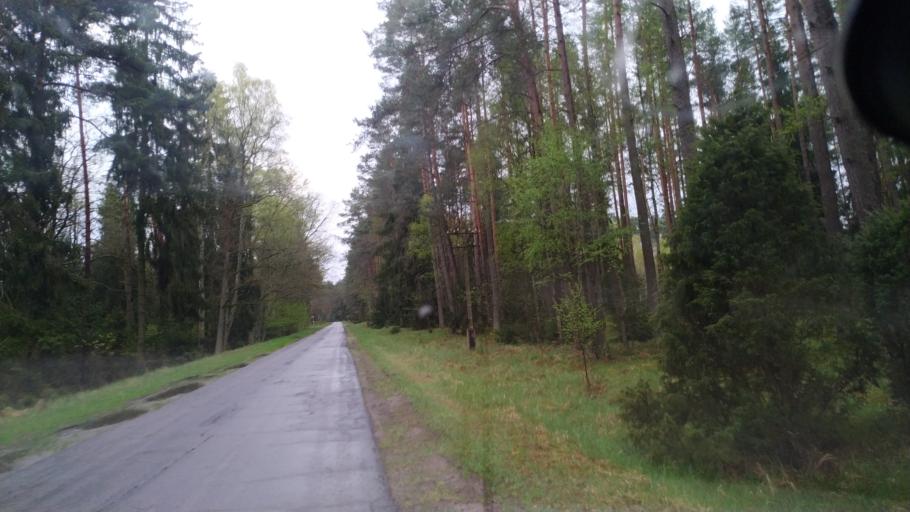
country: PL
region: Pomeranian Voivodeship
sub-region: Powiat starogardzki
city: Osiek
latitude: 53.6596
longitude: 18.4851
